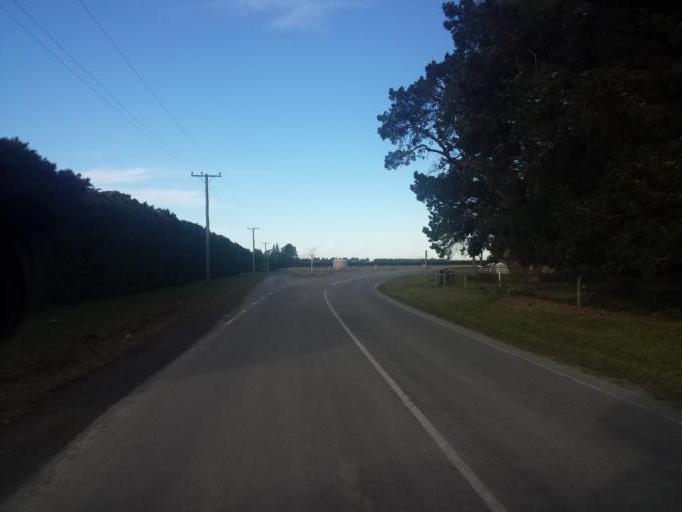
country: NZ
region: Canterbury
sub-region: Ashburton District
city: Methven
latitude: -43.6023
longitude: 171.5662
